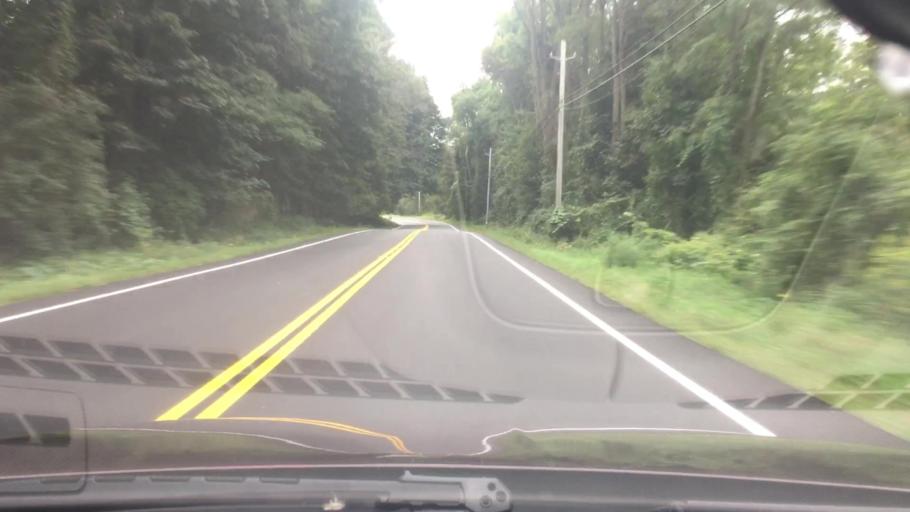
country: US
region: New York
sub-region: Dutchess County
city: Millbrook
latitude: 41.8162
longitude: -73.6297
